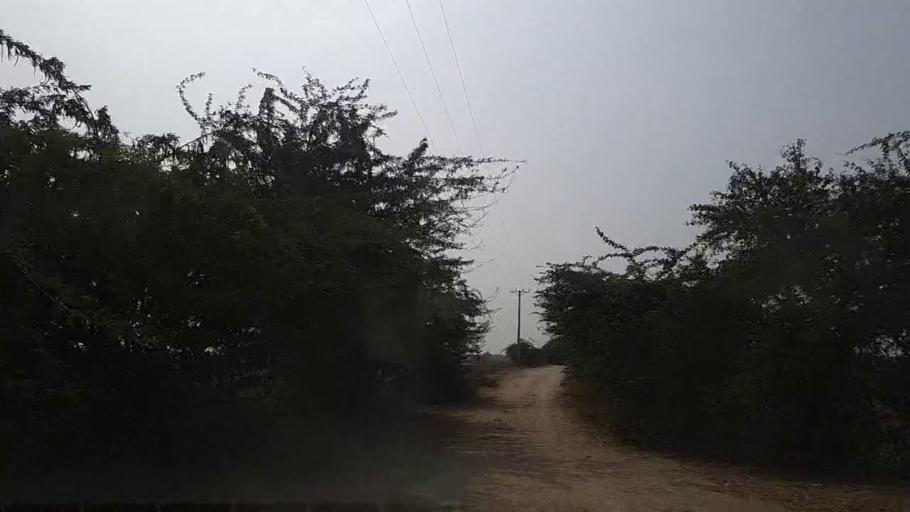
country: PK
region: Sindh
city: Mirpur Sakro
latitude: 24.6151
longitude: 67.7319
